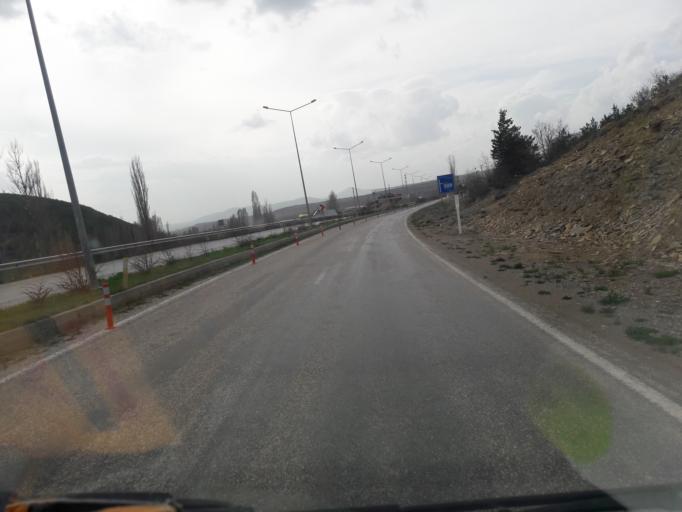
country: TR
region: Gumushane
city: Siran
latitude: 40.1770
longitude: 39.1291
